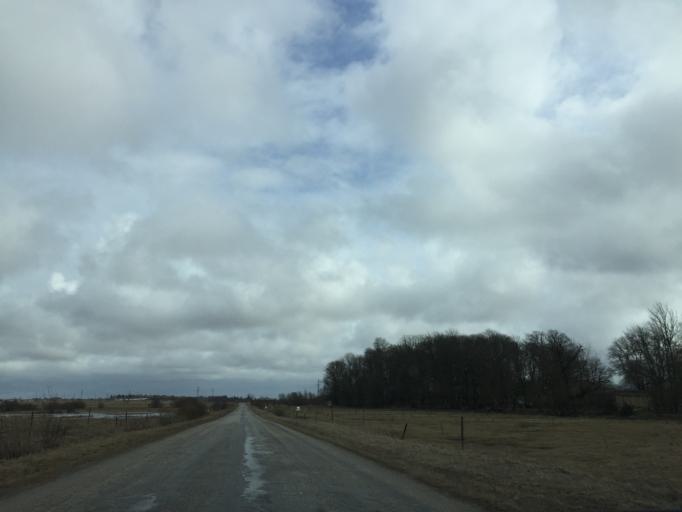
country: EE
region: Laeaene
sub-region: Lihula vald
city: Lihula
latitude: 58.7276
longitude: 23.8992
